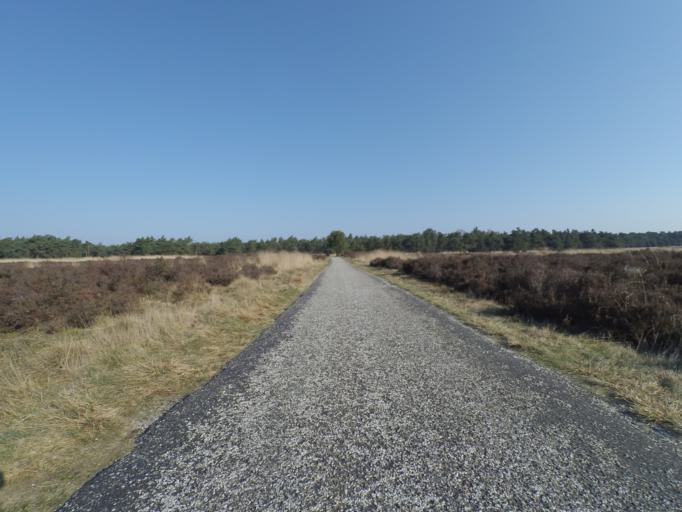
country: NL
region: Gelderland
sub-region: Gemeente Arnhem
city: Hoogkamp
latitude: 52.0669
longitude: 5.8467
